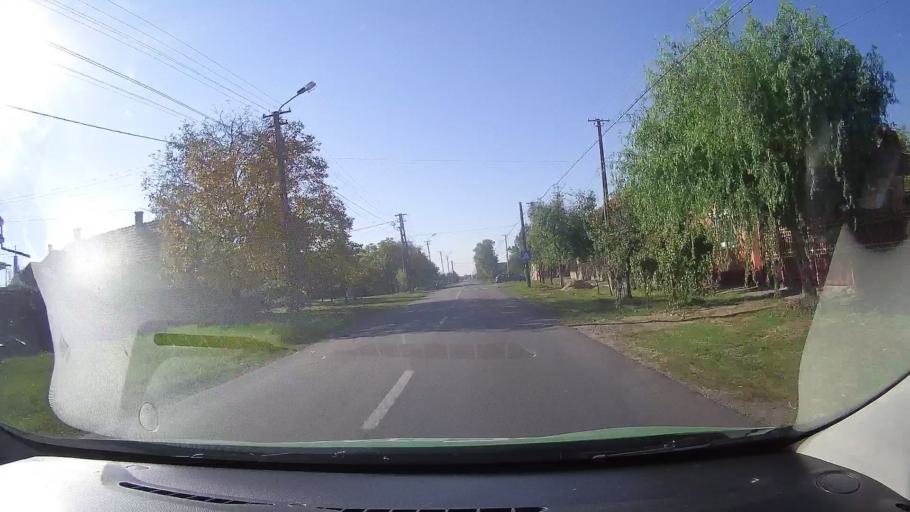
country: RO
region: Satu Mare
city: Carei
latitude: 47.6737
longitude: 22.4675
